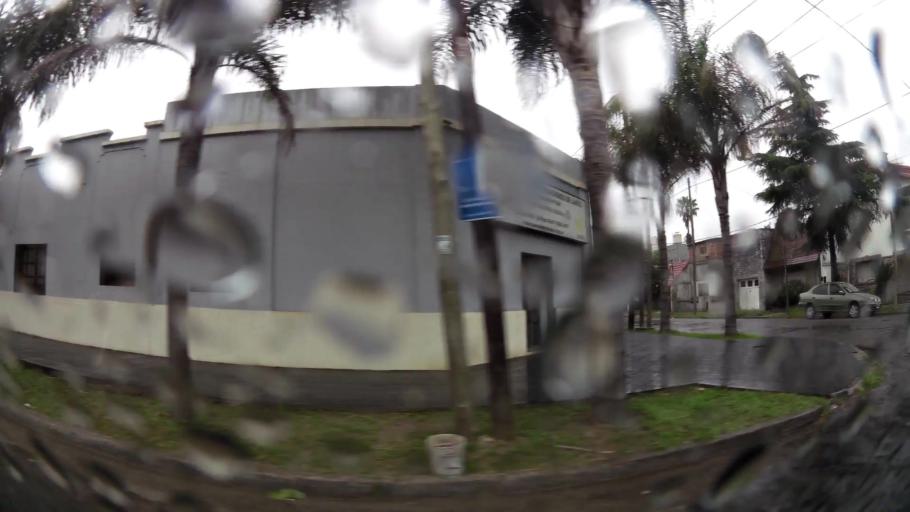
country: AR
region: Buenos Aires
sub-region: Partido de Lanus
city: Lanus
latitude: -34.7035
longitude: -58.4050
